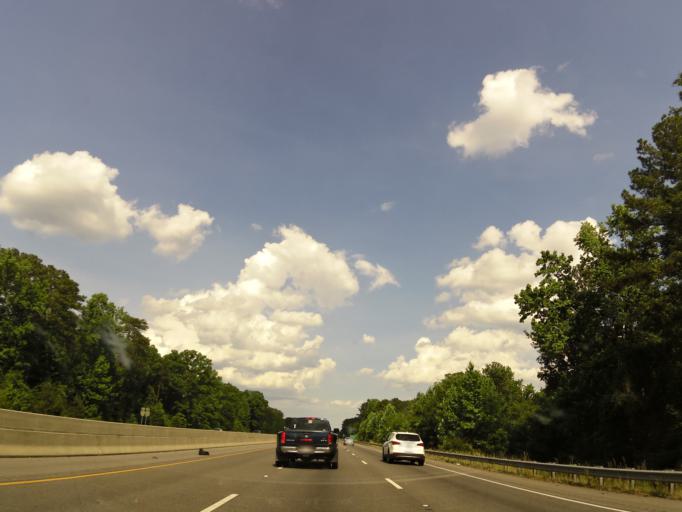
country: US
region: Alabama
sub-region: Tuscaloosa County
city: Coaling
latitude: 33.1897
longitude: -87.3100
